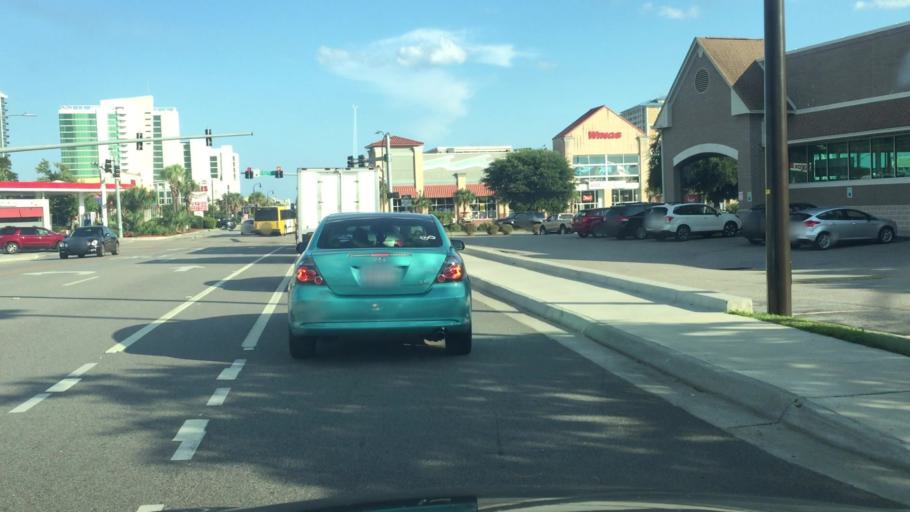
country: US
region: South Carolina
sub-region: Horry County
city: Myrtle Beach
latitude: 33.6849
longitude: -78.8924
